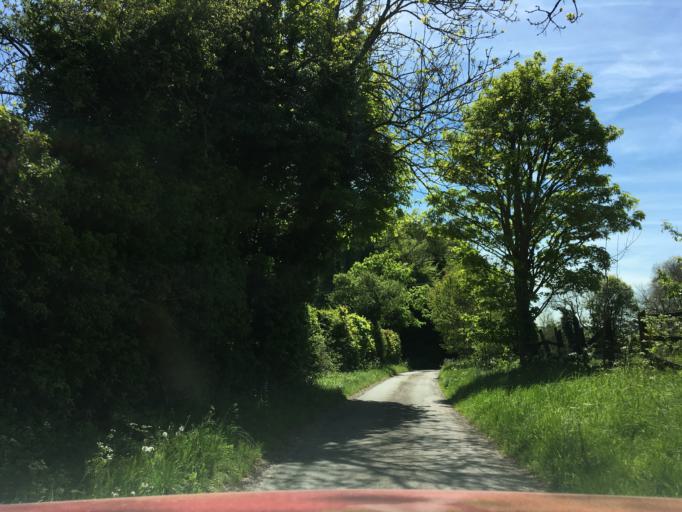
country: GB
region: England
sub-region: Gloucestershire
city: Brimscombe
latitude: 51.7263
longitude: -2.1848
